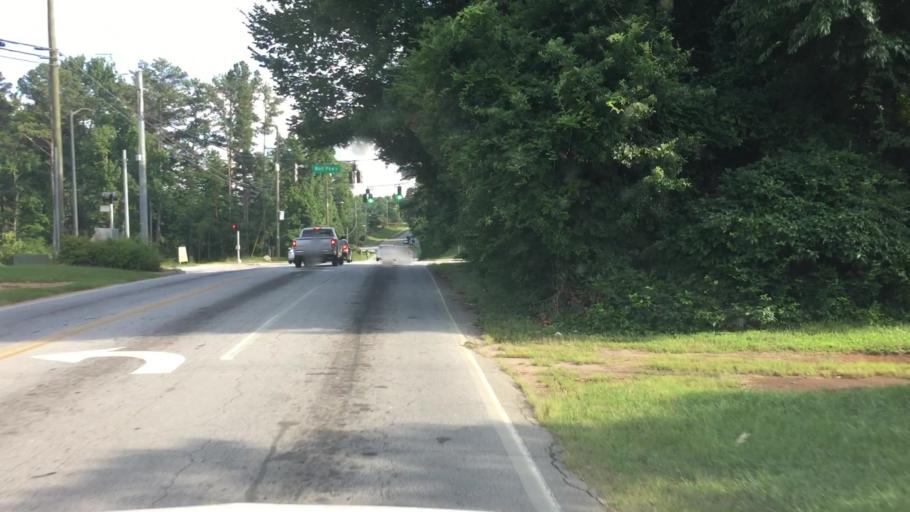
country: US
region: Georgia
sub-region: DeKalb County
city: Lithonia
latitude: 33.6991
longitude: -84.1084
